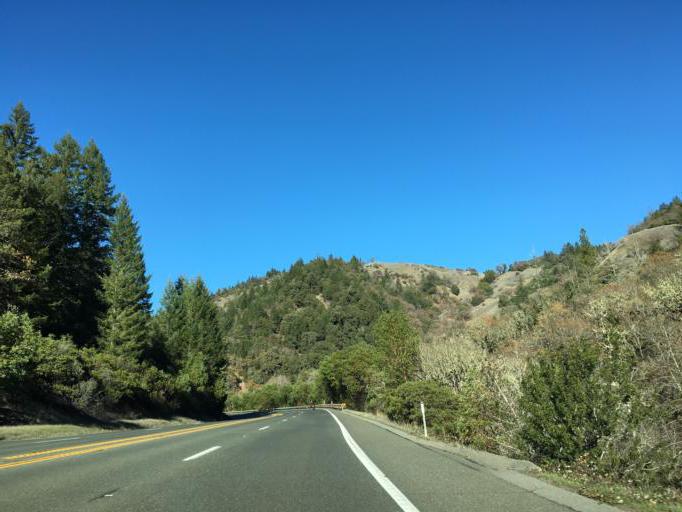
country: US
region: California
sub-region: Mendocino County
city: Laytonville
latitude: 39.5998
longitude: -123.4543
